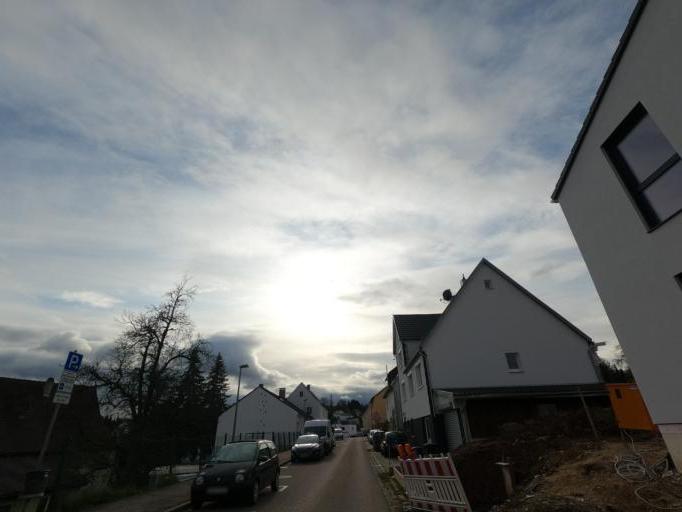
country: DE
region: Baden-Wuerttemberg
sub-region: Regierungsbezirk Stuttgart
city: Albershausen
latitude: 48.6942
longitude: 9.5668
